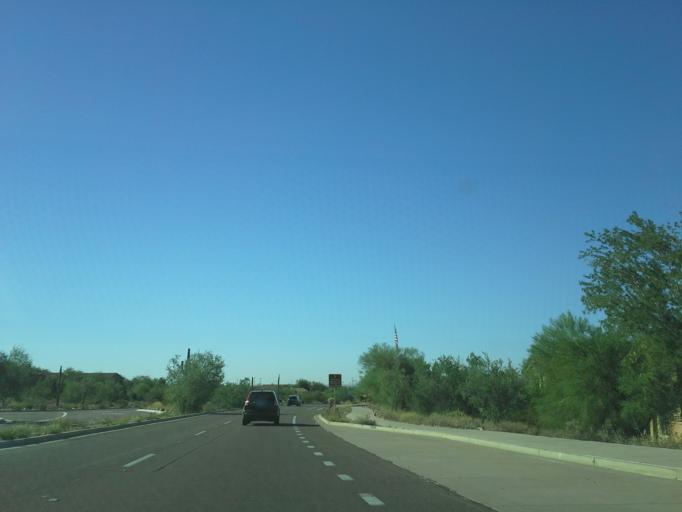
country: US
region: Arizona
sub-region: Maricopa County
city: Scottsdale
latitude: 33.6341
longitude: -111.8604
